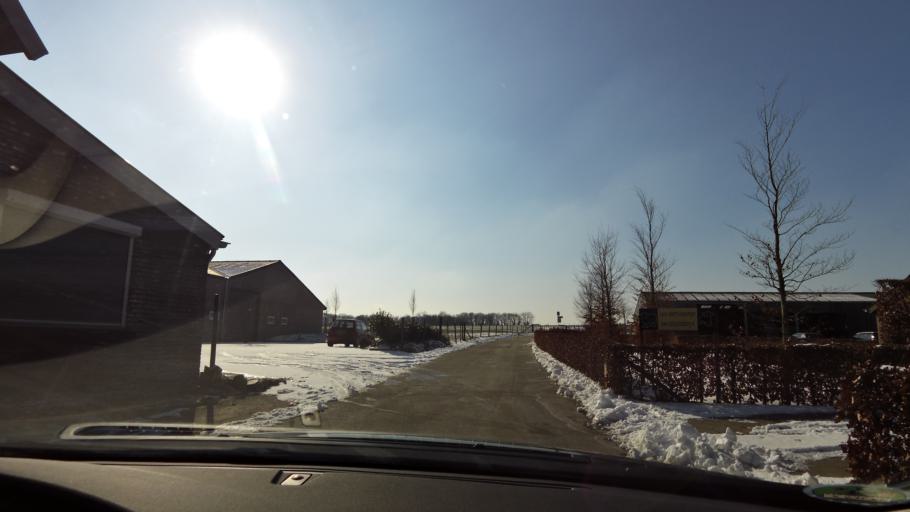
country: NL
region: Limburg
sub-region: Valkenburg aan de Geul
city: Schin op Geul
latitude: 50.8424
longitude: 5.8730
